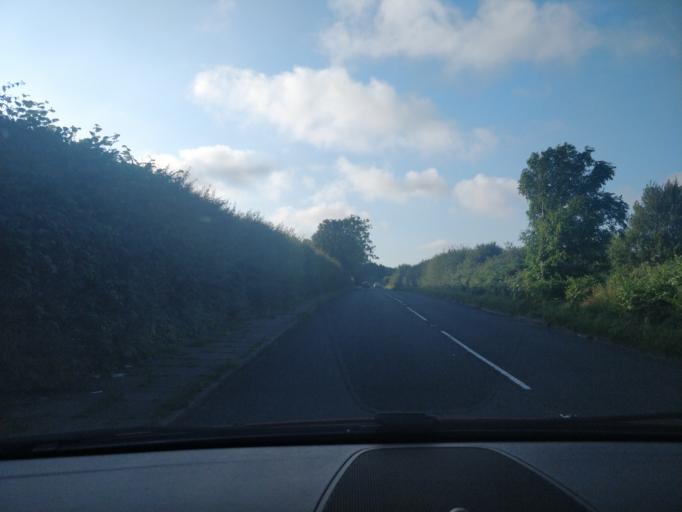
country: GB
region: England
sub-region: Lancashire
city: Skelmersdale
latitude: 53.5503
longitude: -2.7410
